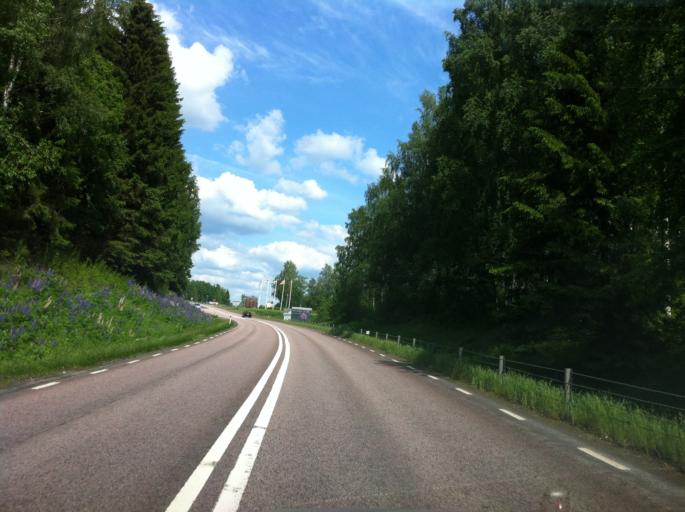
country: SE
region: Vaermland
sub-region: Sunne Kommun
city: Sunne
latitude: 59.8011
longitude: 13.1198
